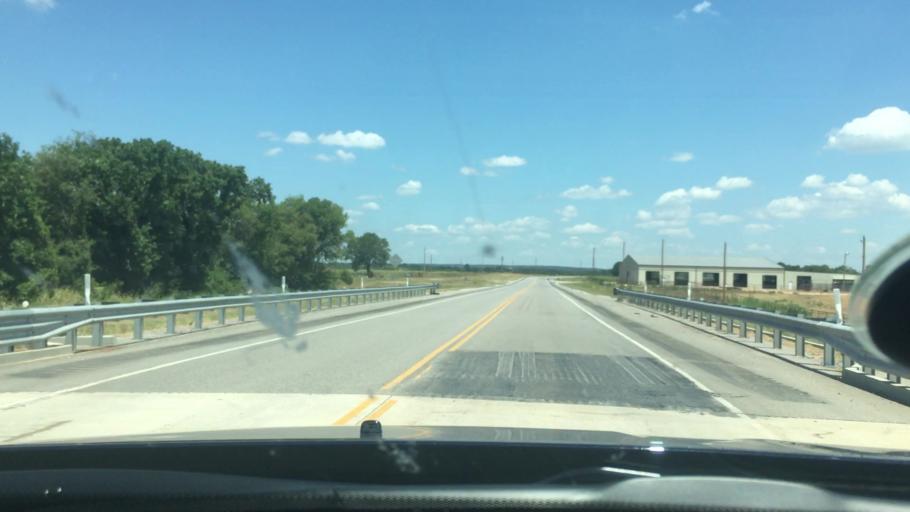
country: US
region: Oklahoma
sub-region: Carter County
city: Dickson
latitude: 34.2354
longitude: -96.9760
